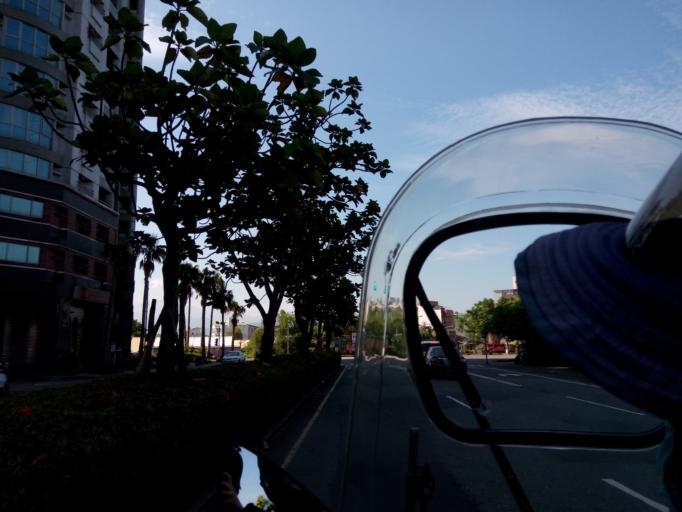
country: TW
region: Taiwan
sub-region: Yilan
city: Yilan
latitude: 24.6794
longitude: 121.7561
